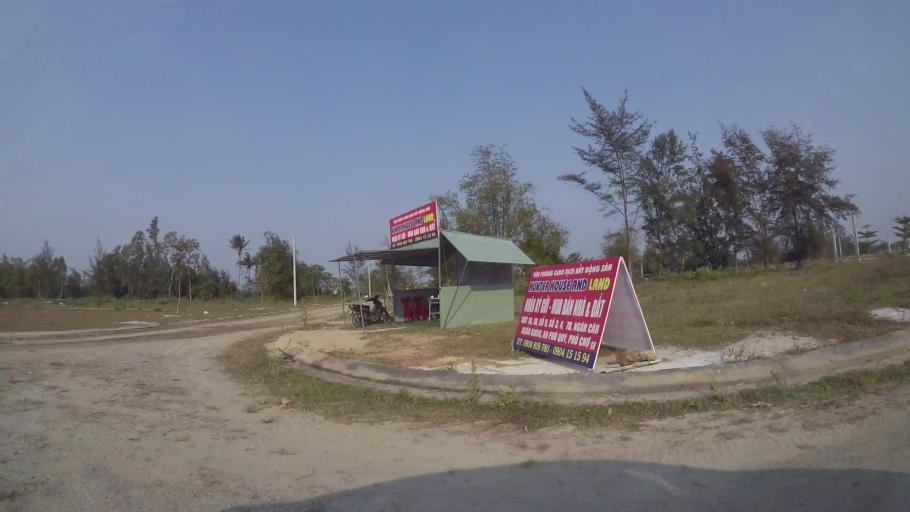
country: VN
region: Da Nang
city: Ngu Hanh Son
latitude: 15.9626
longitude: 108.2647
